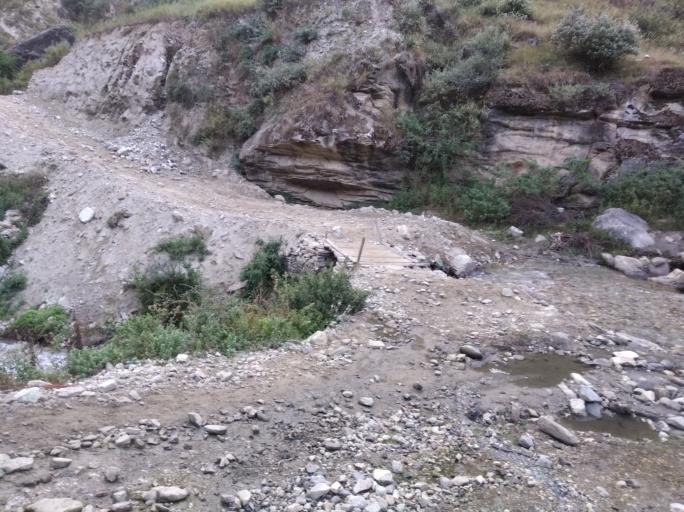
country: NP
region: Western Region
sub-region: Dhawalagiri Zone
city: Jomsom
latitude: 28.8792
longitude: 82.9908
